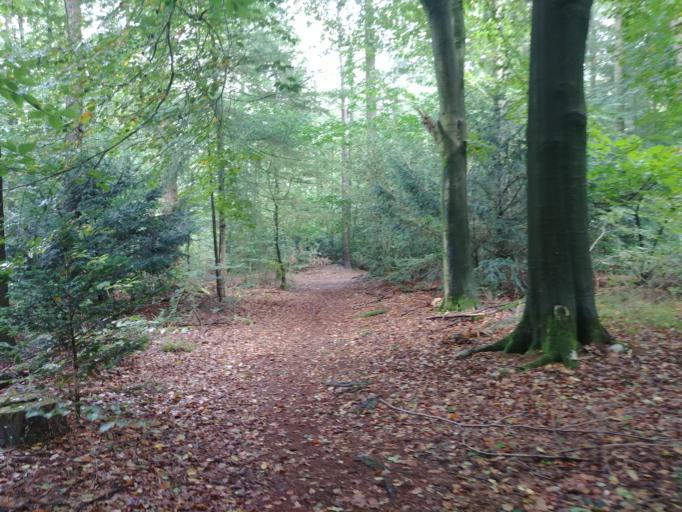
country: NL
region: Gelderland
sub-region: Gemeente Renkum
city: Doorwerth
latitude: 51.9909
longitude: 5.8191
